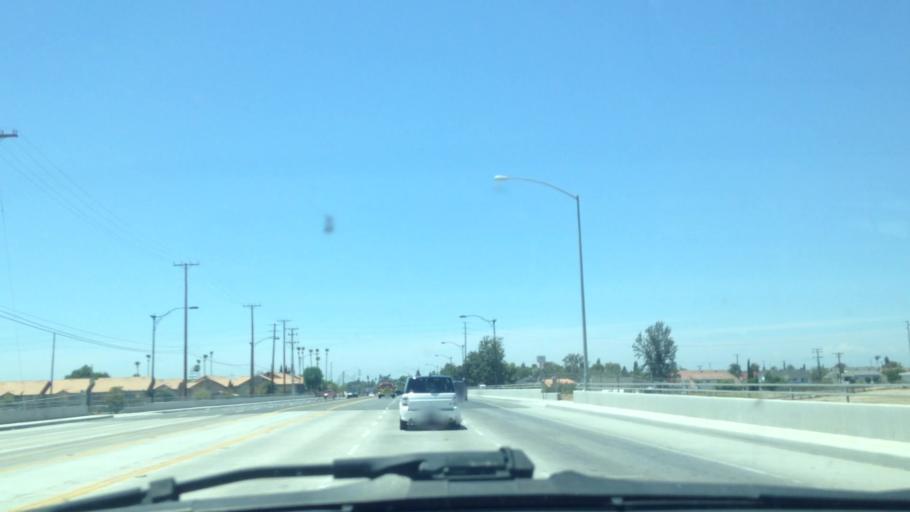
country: US
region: California
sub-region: Orange County
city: Placentia
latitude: 33.8355
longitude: -117.8633
